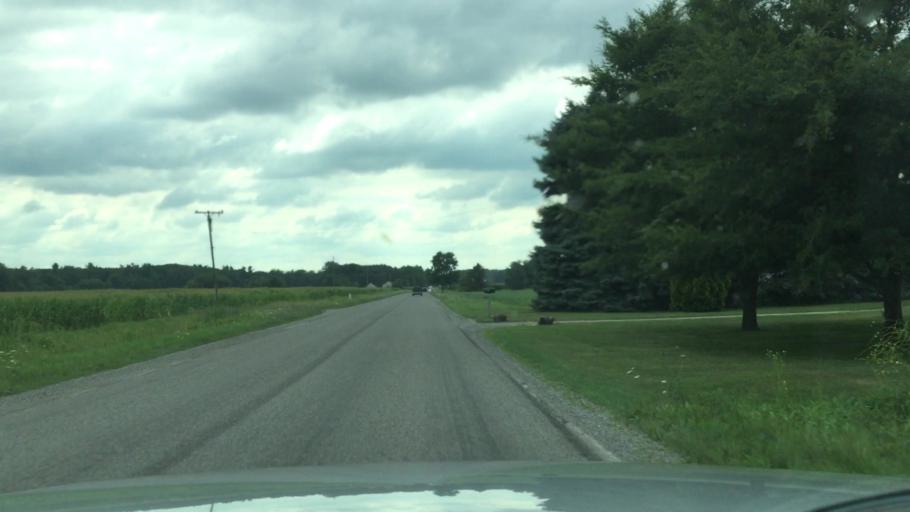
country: US
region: Michigan
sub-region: Saginaw County
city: Frankenmuth
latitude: 43.3218
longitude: -83.7618
